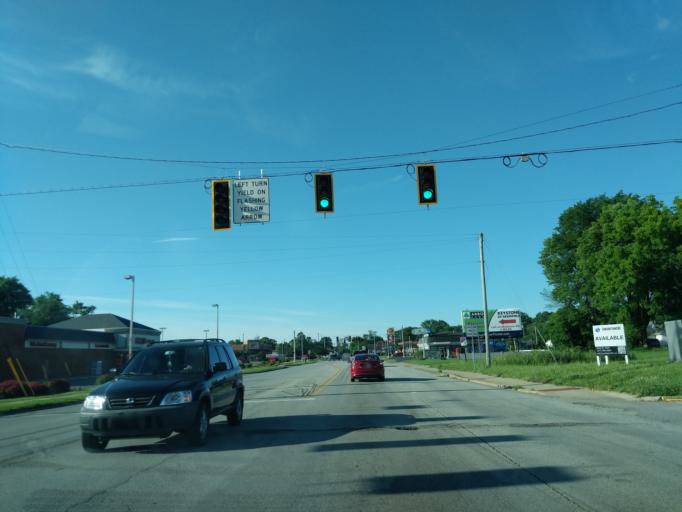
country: US
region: Indiana
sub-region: Hancock County
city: Greenfield
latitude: 39.8011
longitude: -85.7698
